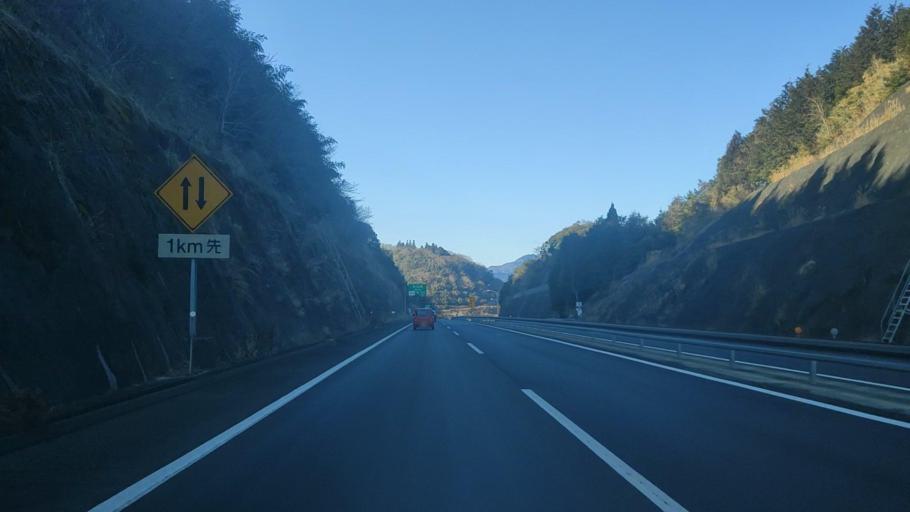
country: JP
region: Oita
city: Bungo-Takada-shi
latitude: 33.4467
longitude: 131.3789
